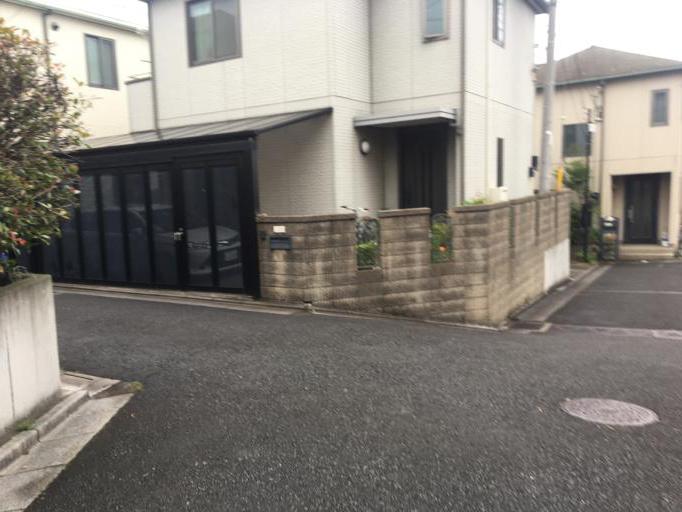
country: JP
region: Saitama
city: Shimotoda
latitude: 35.8469
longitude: 139.6609
